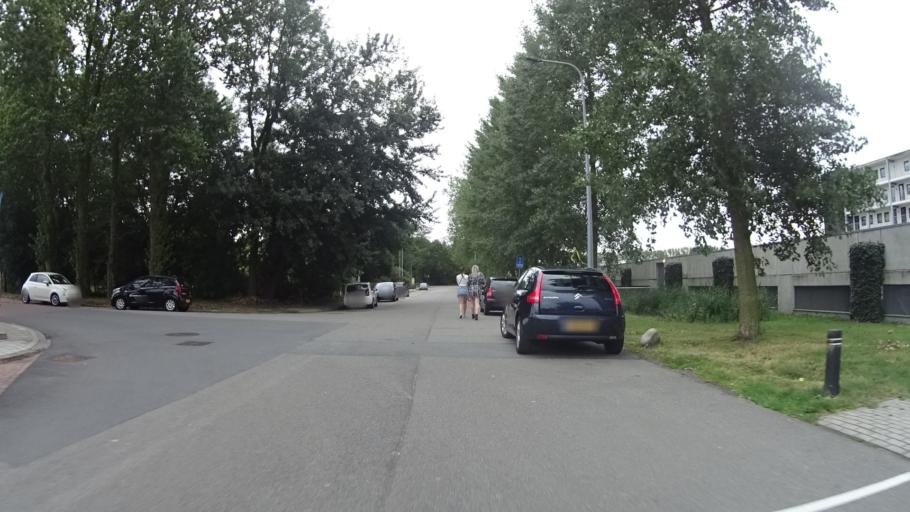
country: NL
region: Groningen
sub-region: Gemeente Groningen
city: Oosterpark
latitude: 53.2250
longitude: 6.5996
